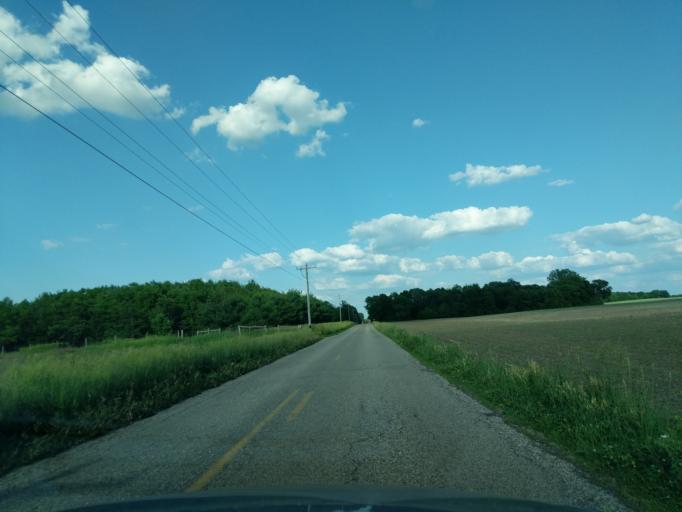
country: US
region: Indiana
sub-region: Kosciusko County
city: North Webster
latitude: 41.3025
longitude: -85.6049
